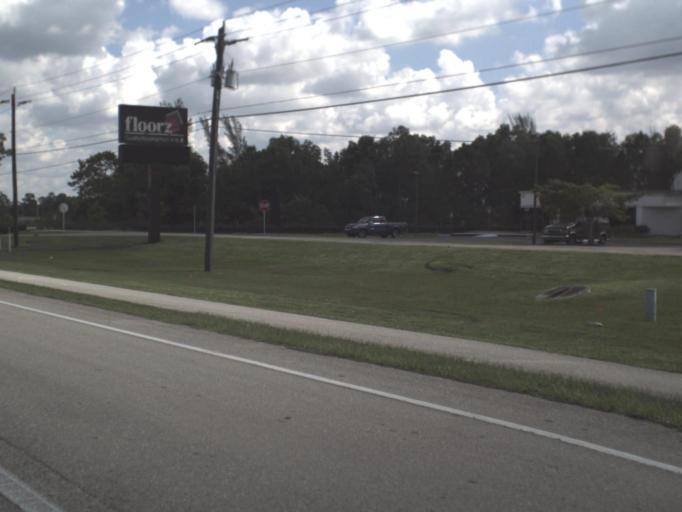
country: US
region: Florida
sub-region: Lee County
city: Fort Myers
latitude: 26.6068
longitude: -81.8244
